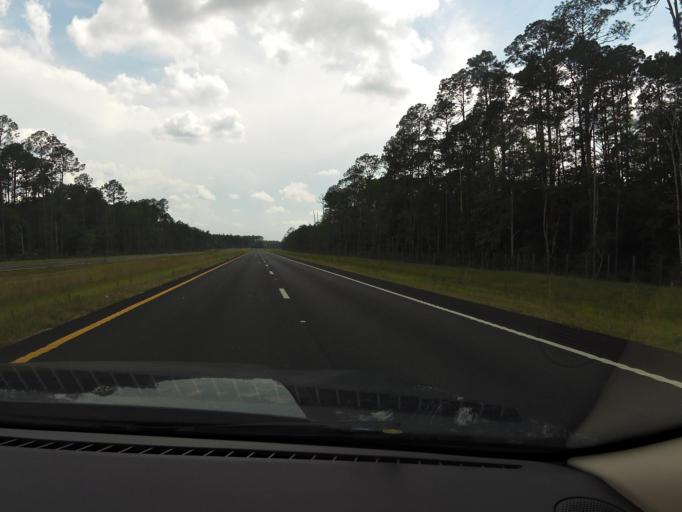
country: US
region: Florida
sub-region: Duval County
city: Baldwin
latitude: 30.3192
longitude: -81.9737
